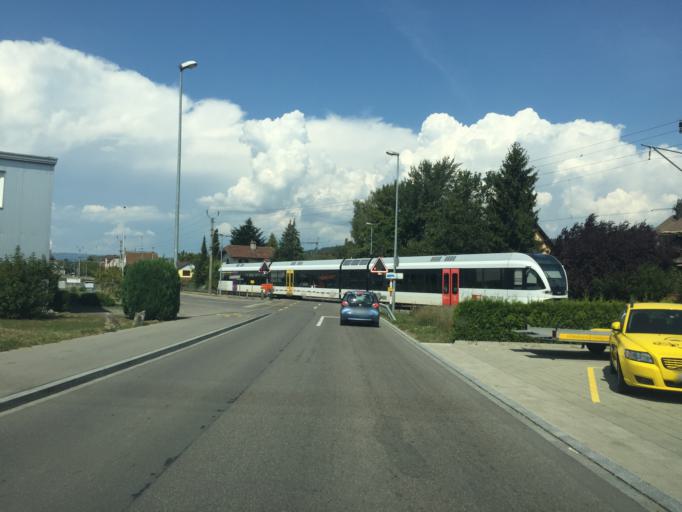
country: CH
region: Thurgau
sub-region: Frauenfeld District
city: Diessenhofen
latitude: 47.6829
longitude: 8.7580
